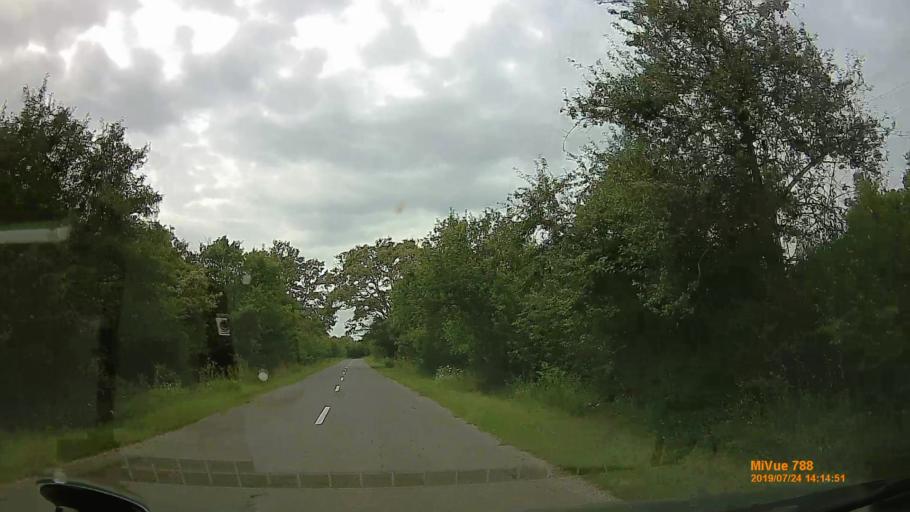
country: UA
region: Zakarpattia
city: Batiovo
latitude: 48.3214
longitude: 22.3141
